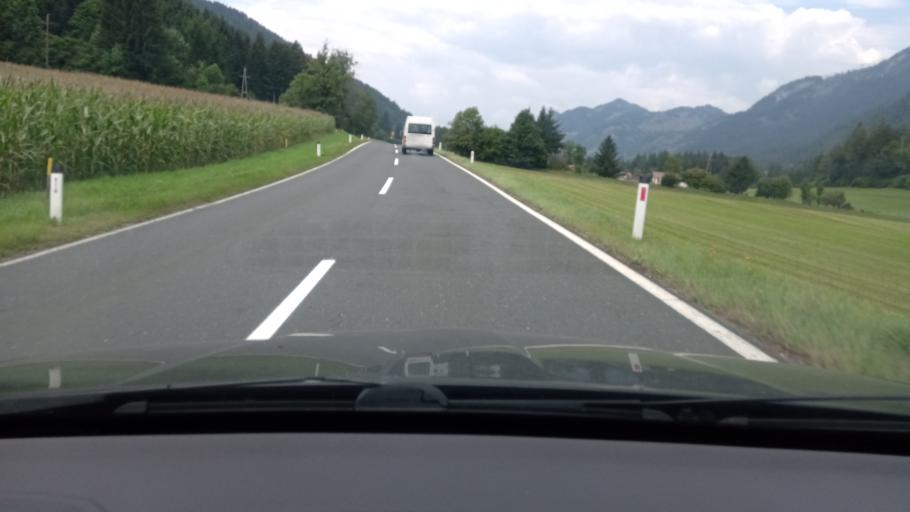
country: AT
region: Carinthia
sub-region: Politischer Bezirk Hermagor
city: Hermagor
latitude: 46.6414
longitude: 13.3421
